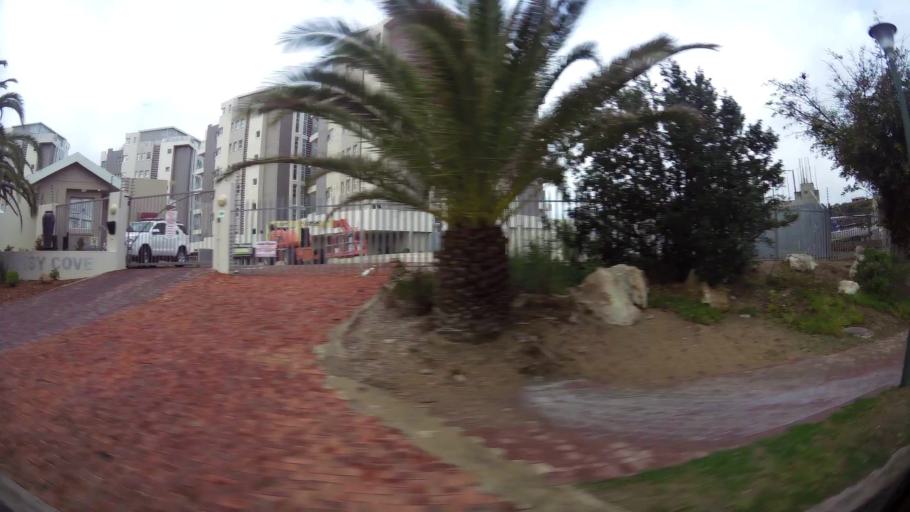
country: ZA
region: Western Cape
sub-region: Eden District Municipality
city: Mossel Bay
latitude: -34.1626
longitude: 22.1090
